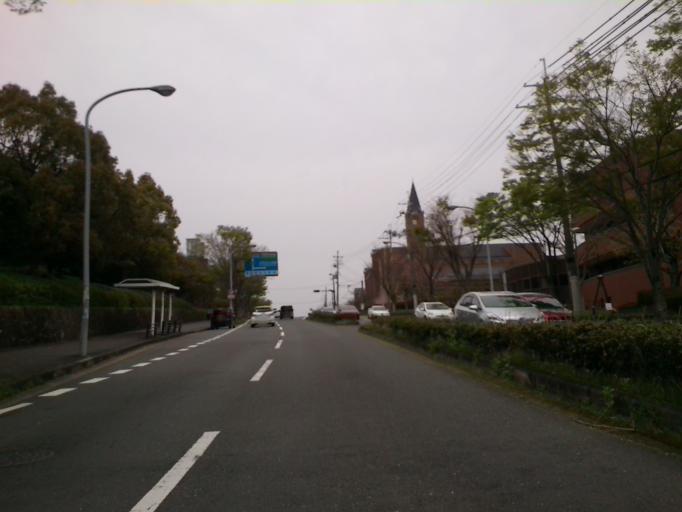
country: JP
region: Kyoto
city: Tanabe
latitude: 34.8015
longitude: 135.7728
